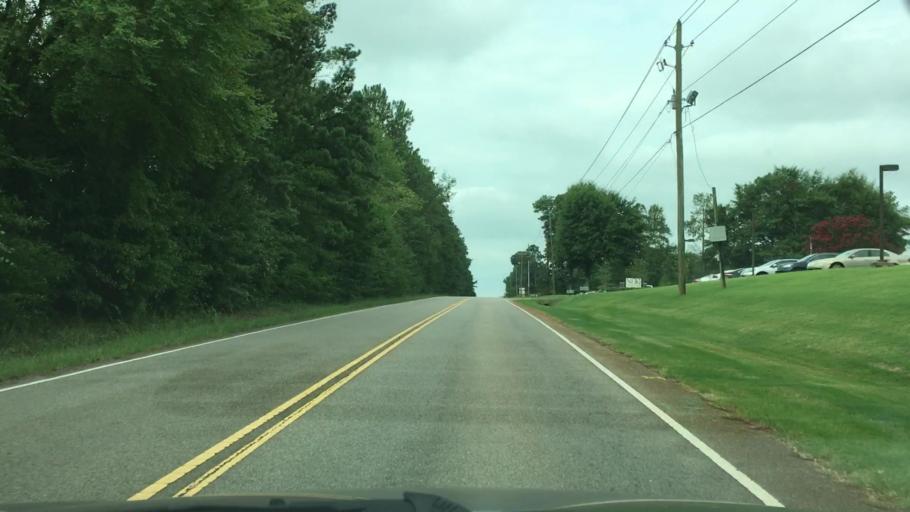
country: US
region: South Carolina
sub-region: Aiken County
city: Belvedere
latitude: 33.5613
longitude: -81.9423
